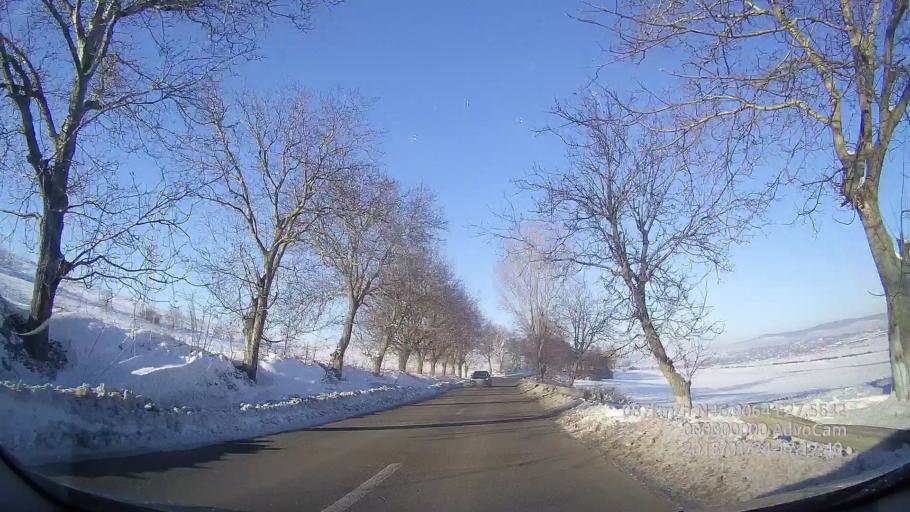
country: RO
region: Iasi
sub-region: Comuna Scanteia
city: Scanteia
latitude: 46.9071
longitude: 27.5641
